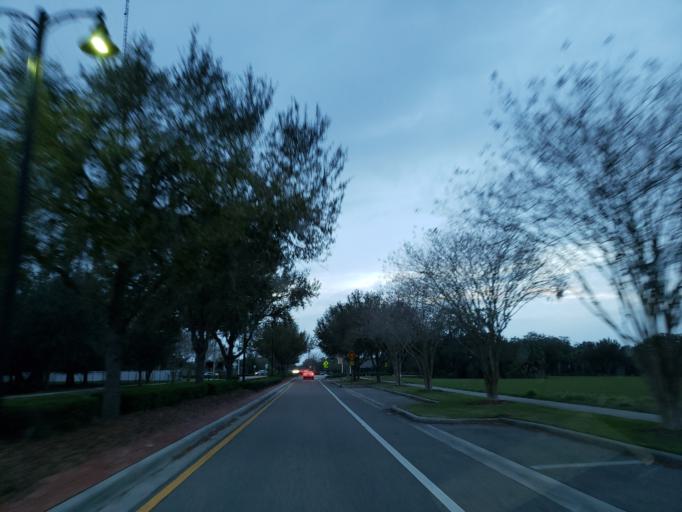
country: US
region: Florida
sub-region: Hillsborough County
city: Bloomingdale
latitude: 27.8501
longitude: -82.2596
